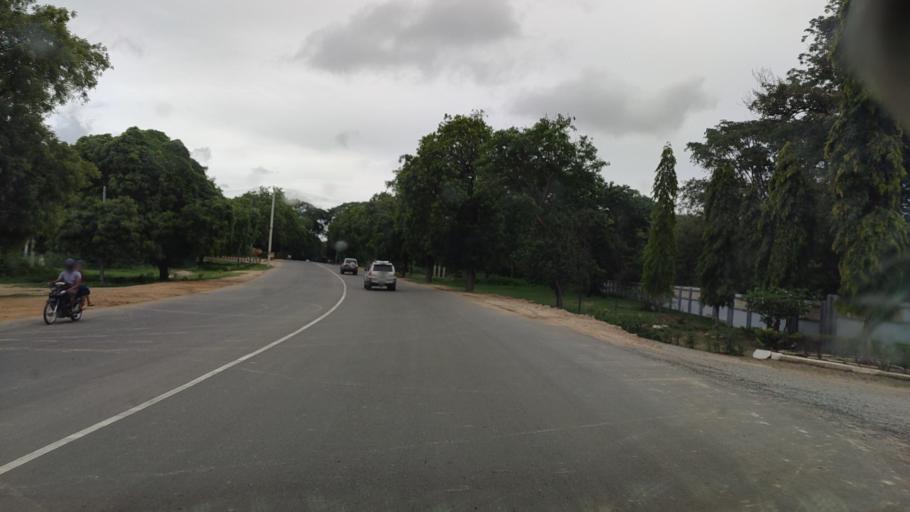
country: MM
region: Mandalay
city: Meiktila
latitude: 20.8606
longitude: 95.8702
